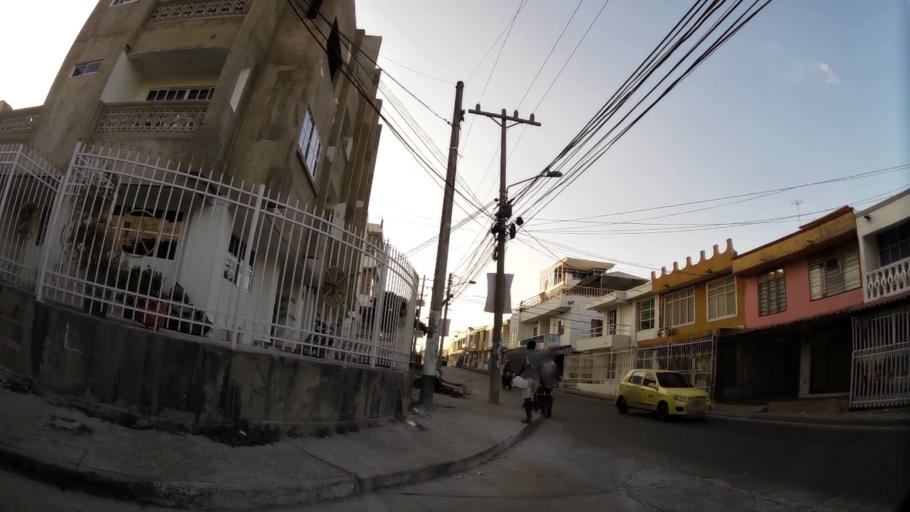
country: CO
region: Bolivar
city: Cartagena
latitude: 10.3899
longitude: -75.4825
